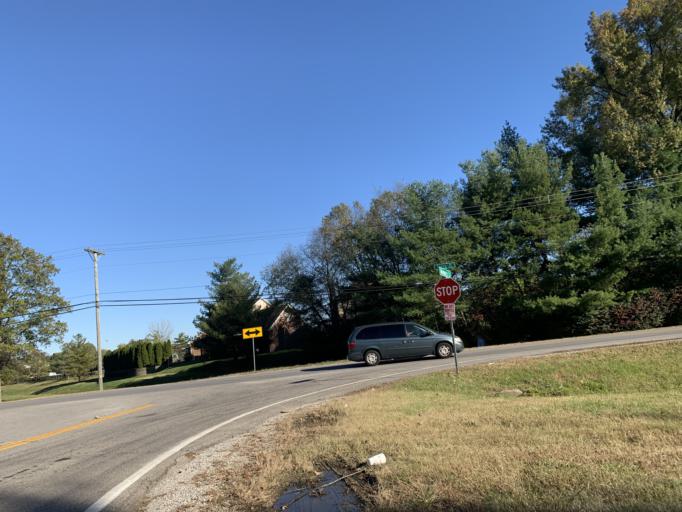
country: US
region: Kentucky
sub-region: Jefferson County
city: Pleasure Ridge Park
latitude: 38.1566
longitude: -85.8684
